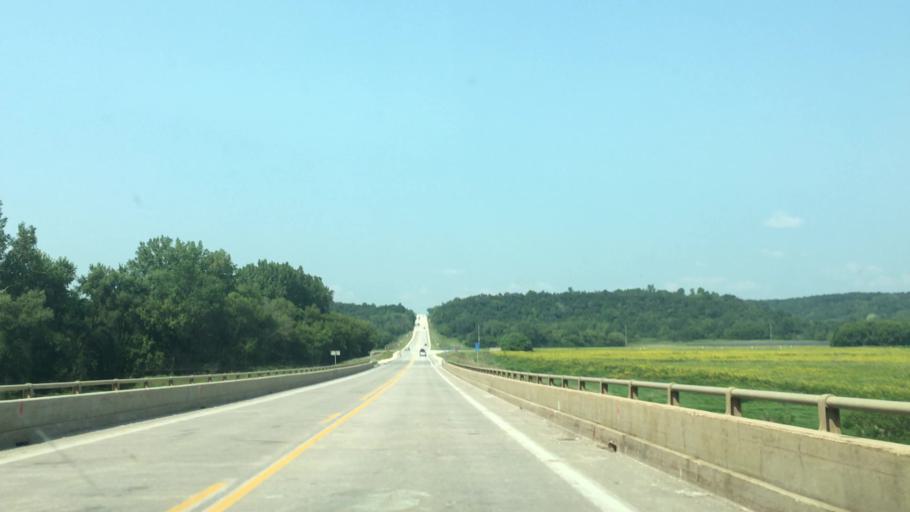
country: US
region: Iowa
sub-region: Winneshiek County
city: Decorah
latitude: 43.3154
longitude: -91.8144
